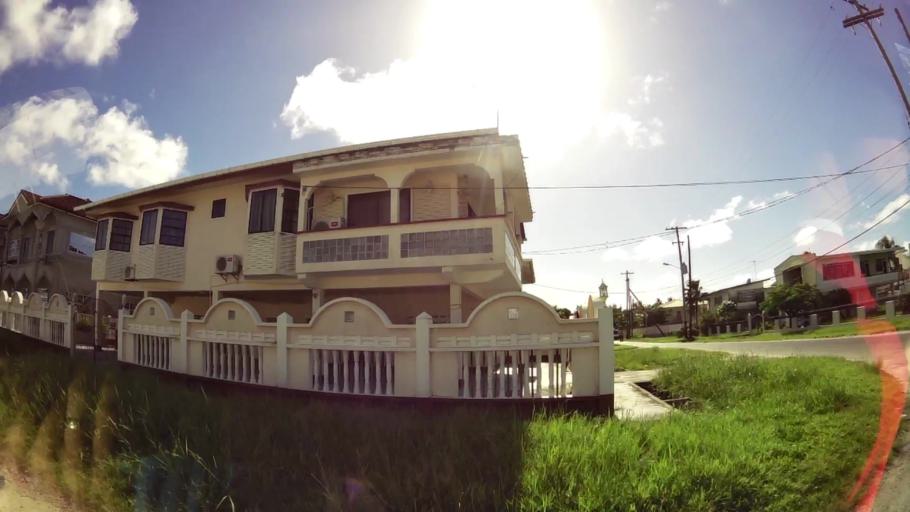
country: GY
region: Demerara-Mahaica
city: Georgetown
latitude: 6.8175
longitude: -58.1299
